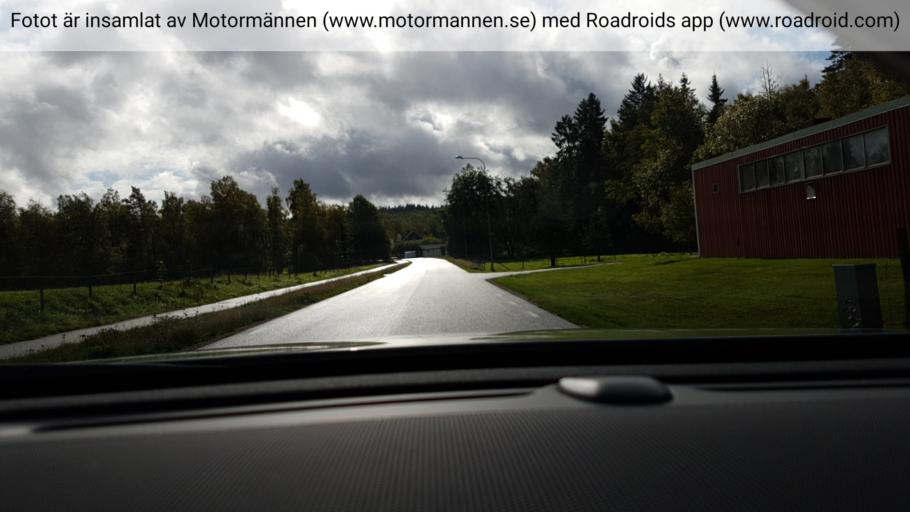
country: SE
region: Vaestra Goetaland
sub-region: Svenljunga Kommun
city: Svenljunga
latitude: 57.4175
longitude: 12.9668
